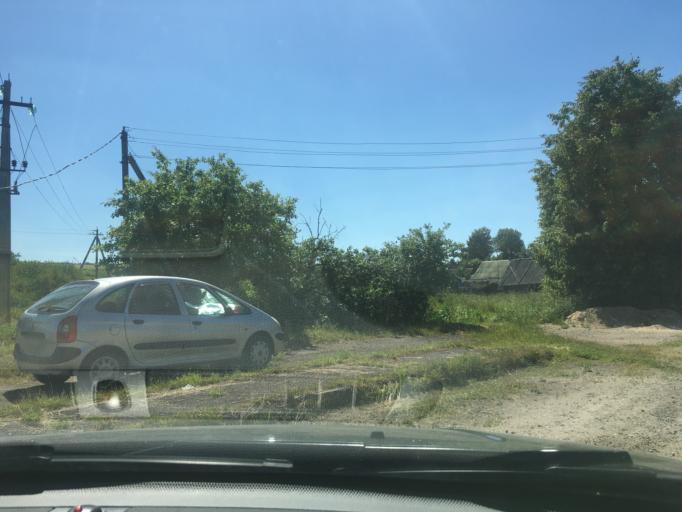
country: BY
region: Grodnenskaya
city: Hal'shany
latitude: 54.2591
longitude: 25.9838
